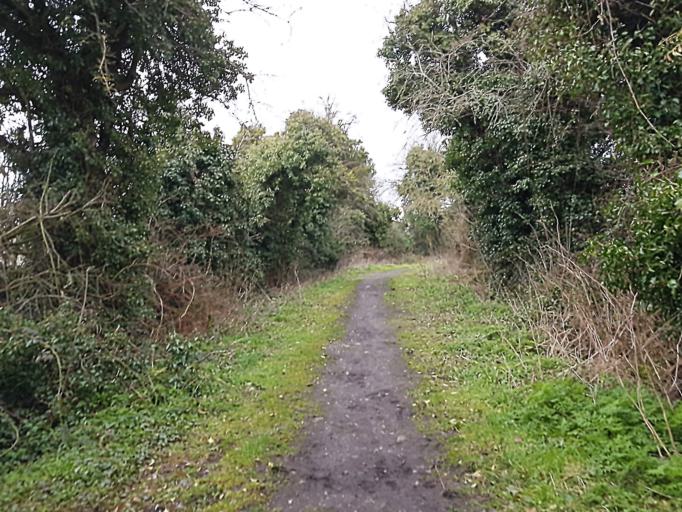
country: IE
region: Leinster
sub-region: Kildare
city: Clane
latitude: 53.2941
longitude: -6.6984
